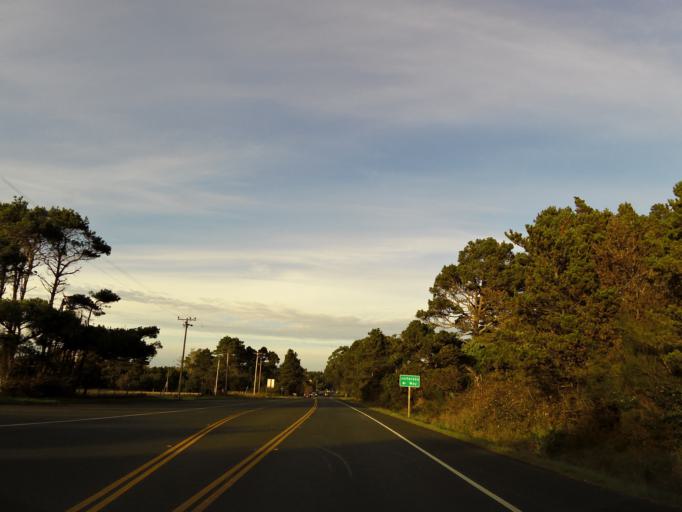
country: US
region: California
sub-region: Mendocino County
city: Fort Bragg
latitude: 39.3843
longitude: -123.8136
